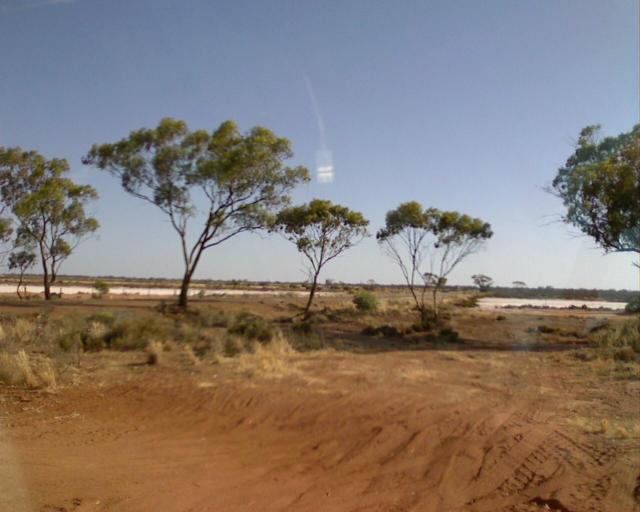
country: AU
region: Western Australia
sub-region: Wongan-Ballidu
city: Wongan Hills
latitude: -30.0188
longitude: 116.8056
